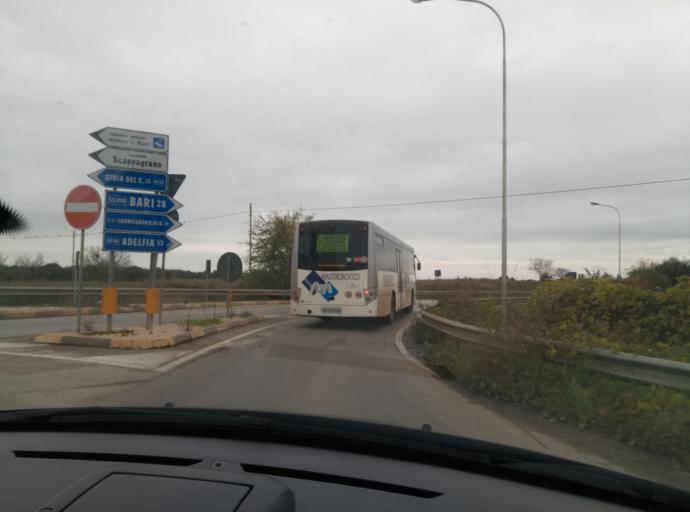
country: IT
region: Apulia
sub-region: Provincia di Bari
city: Acquaviva delle Fonti
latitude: 40.9005
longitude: 16.8329
